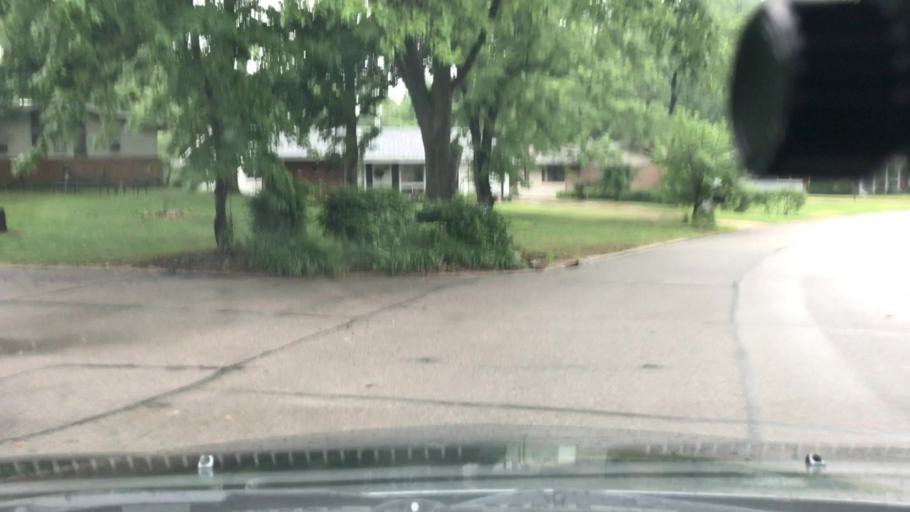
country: US
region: Missouri
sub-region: Saint Louis County
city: Maryland Heights
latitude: 38.6927
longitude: -90.4568
